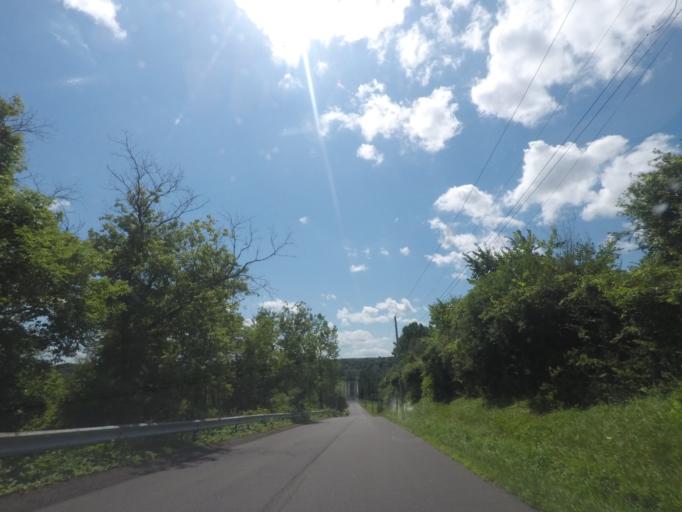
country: US
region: New York
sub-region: Albany County
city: Voorheesville
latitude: 42.7181
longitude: -73.9500
